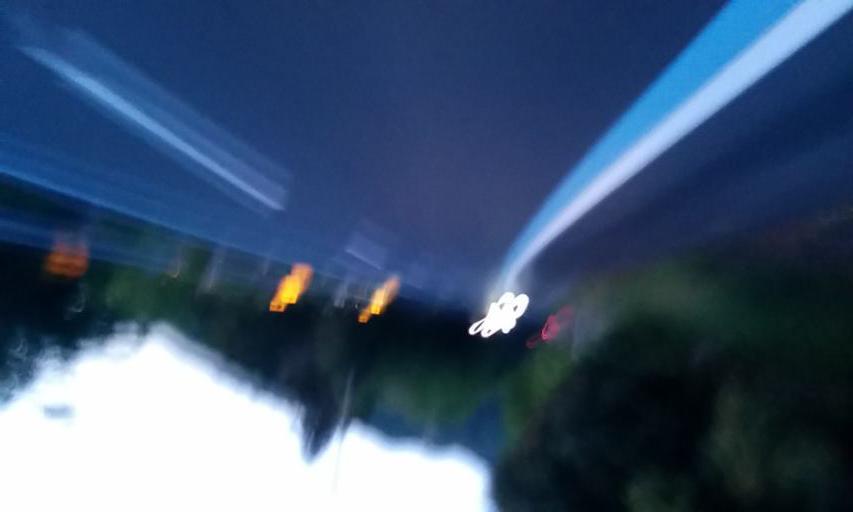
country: JP
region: Ehime
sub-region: Nishiuwa-gun
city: Ikata-cho
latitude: 33.5348
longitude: 132.3994
